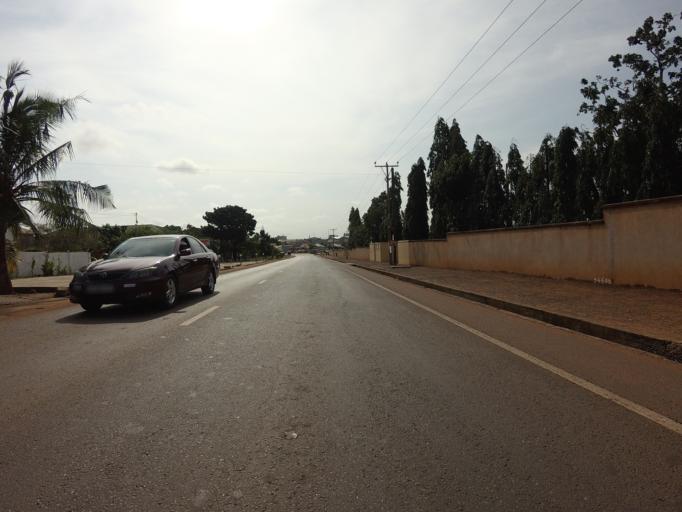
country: GH
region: Greater Accra
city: Nungua
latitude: 5.6451
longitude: -0.0988
